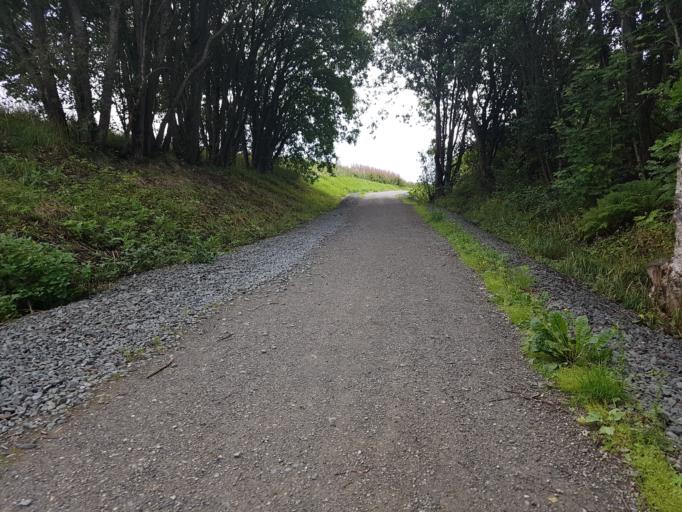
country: NO
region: Sor-Trondelag
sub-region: Trondheim
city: Trondheim
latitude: 63.3843
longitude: 10.4139
